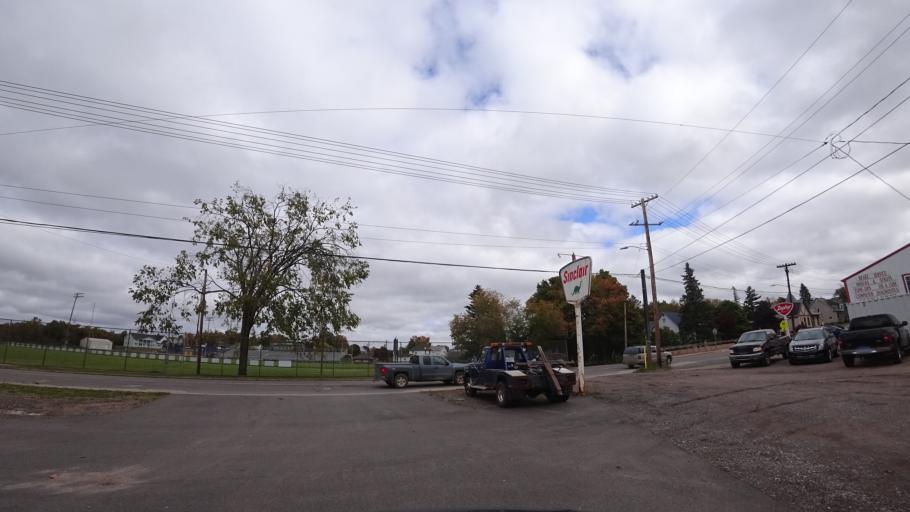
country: US
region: Michigan
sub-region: Marquette County
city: Negaunee
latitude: 46.5050
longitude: -87.6116
